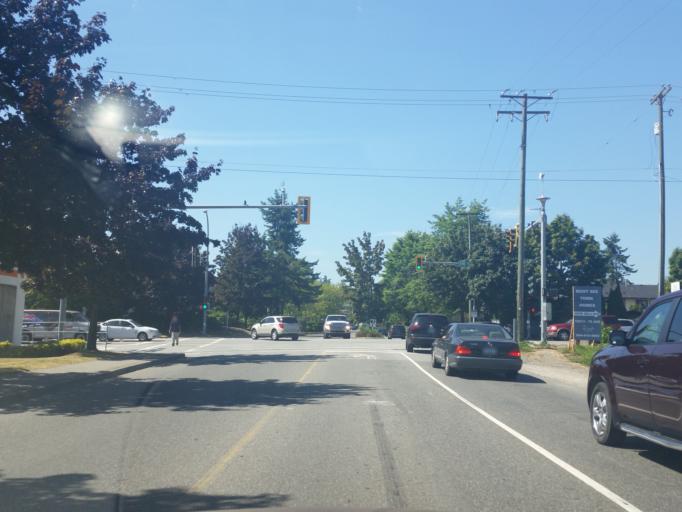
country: CA
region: British Columbia
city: Langley
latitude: 49.1226
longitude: -122.6677
